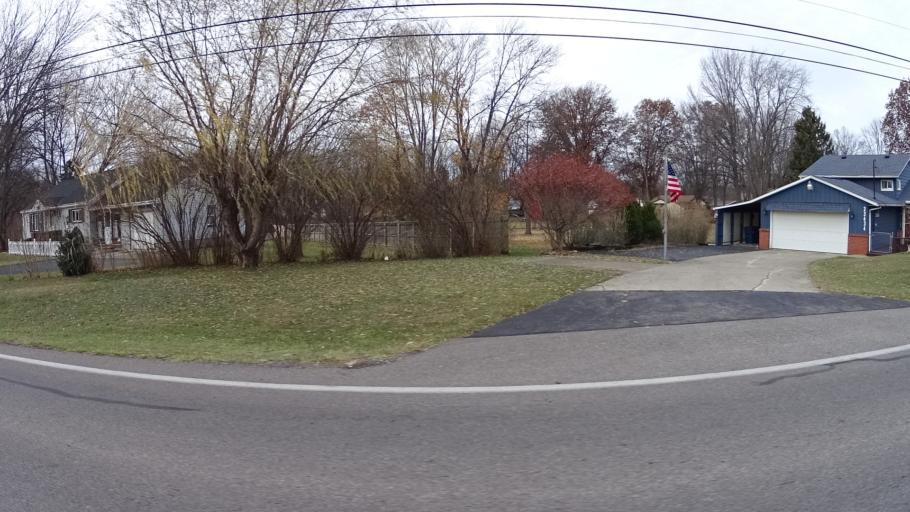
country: US
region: Ohio
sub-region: Lorain County
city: North Ridgeville
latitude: 41.3837
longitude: -81.9876
